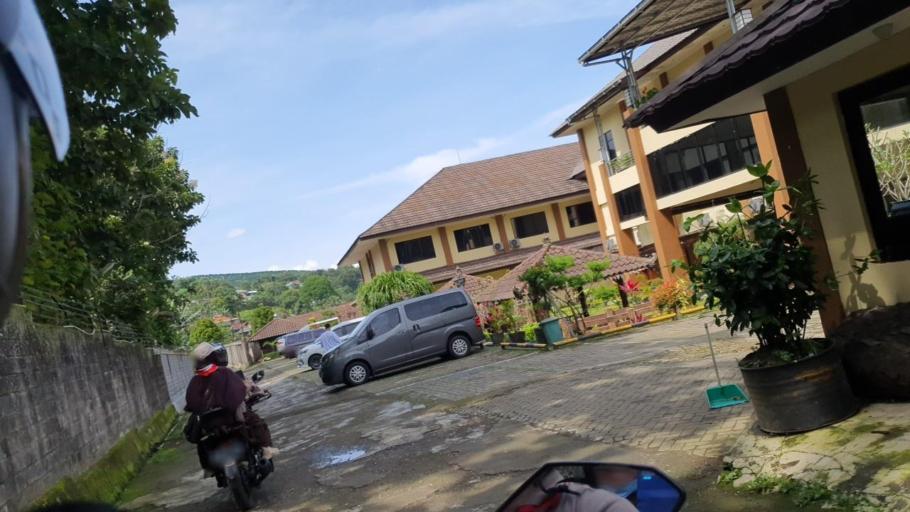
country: ID
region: West Java
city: Caringin
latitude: -6.6512
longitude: 106.9045
